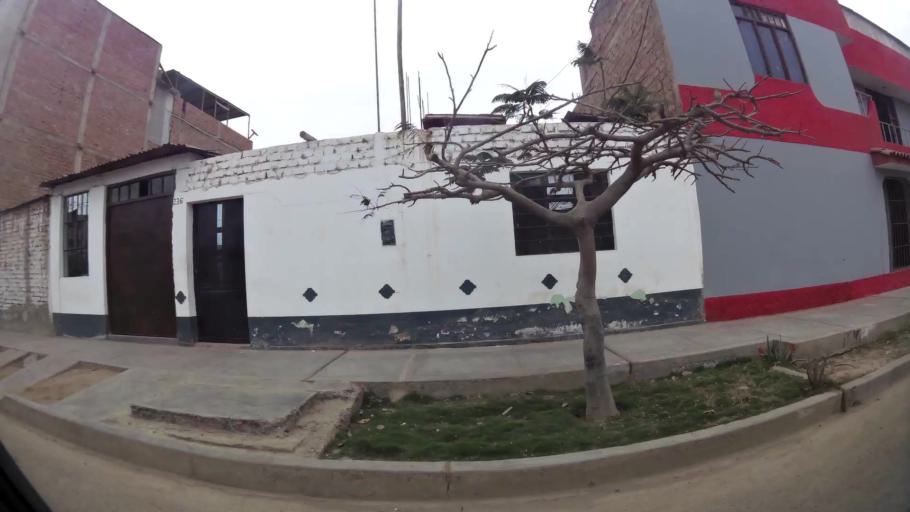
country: PE
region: La Libertad
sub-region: Provincia de Trujillo
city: Buenos Aires
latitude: -8.1399
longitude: -79.0475
